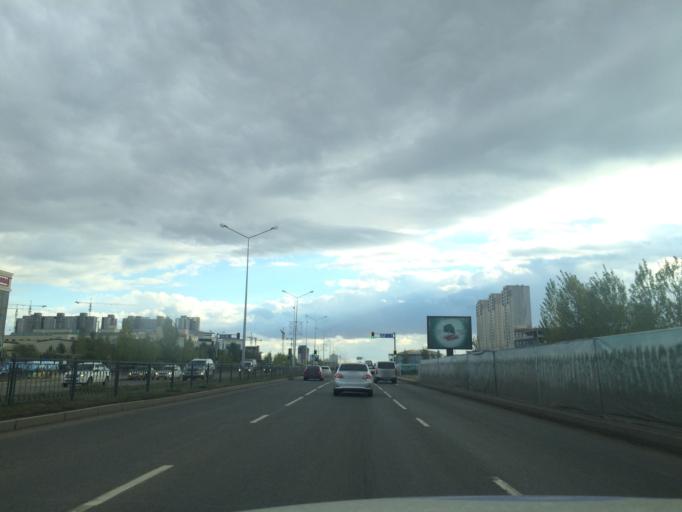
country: KZ
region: Astana Qalasy
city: Astana
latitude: 51.1232
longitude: 71.4032
